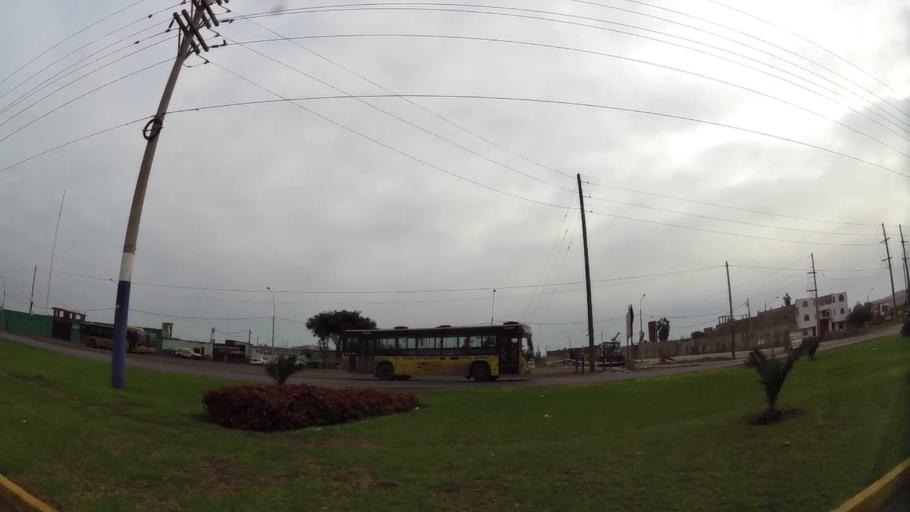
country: PE
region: Lima
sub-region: Lima
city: Surco
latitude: -12.2005
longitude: -76.9961
